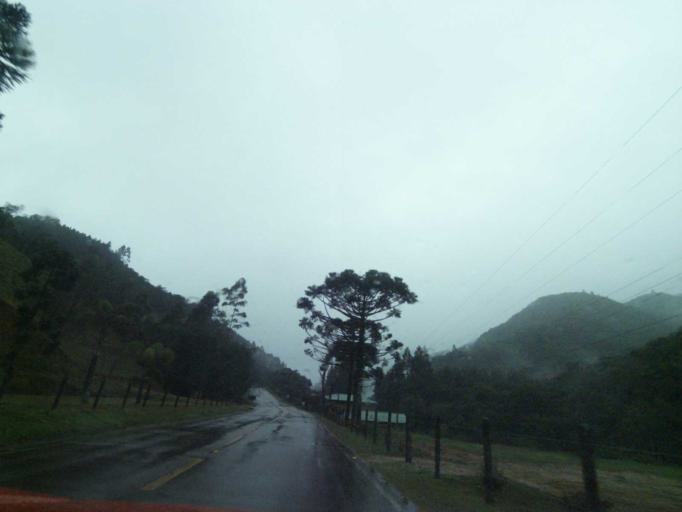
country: BR
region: Santa Catarina
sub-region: Anitapolis
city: Anitapolis
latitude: -27.8269
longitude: -49.0505
